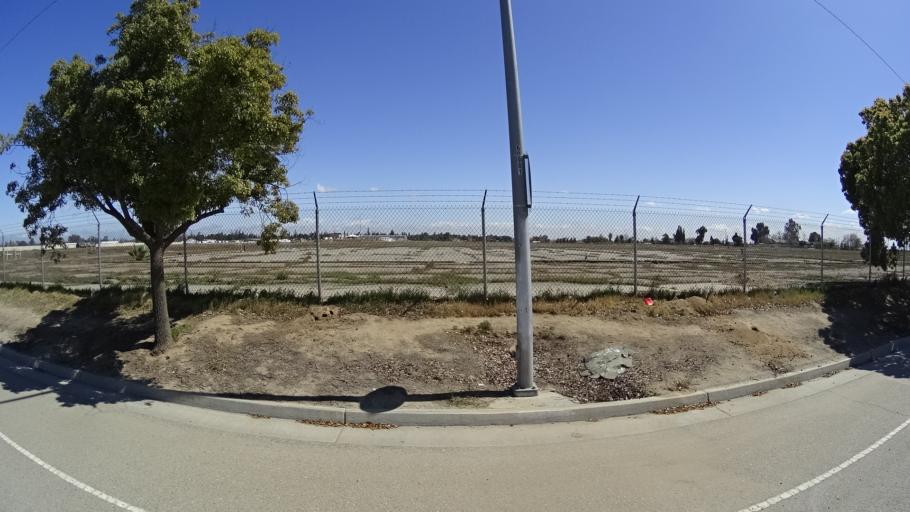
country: US
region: California
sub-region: Fresno County
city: West Park
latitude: 36.7447
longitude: -119.8443
